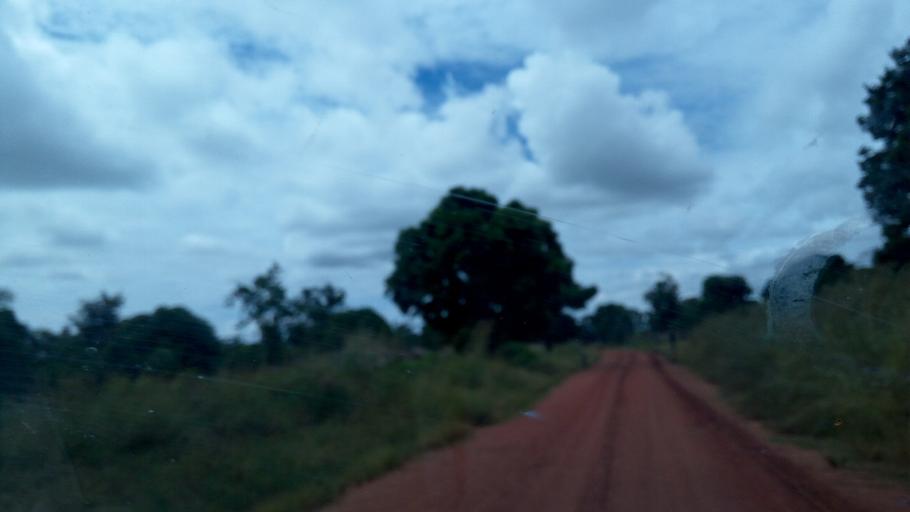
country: CD
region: Katanga
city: Kalemie
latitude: -5.9942
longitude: 29.0728
